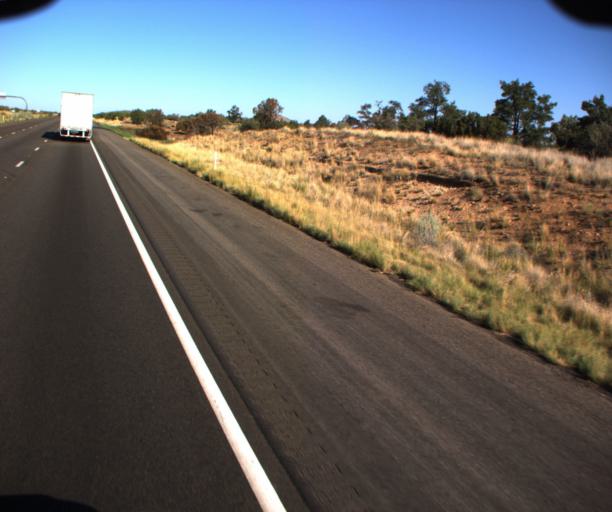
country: US
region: Arizona
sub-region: Mohave County
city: New Kingman-Butler
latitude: 35.1659
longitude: -113.7394
